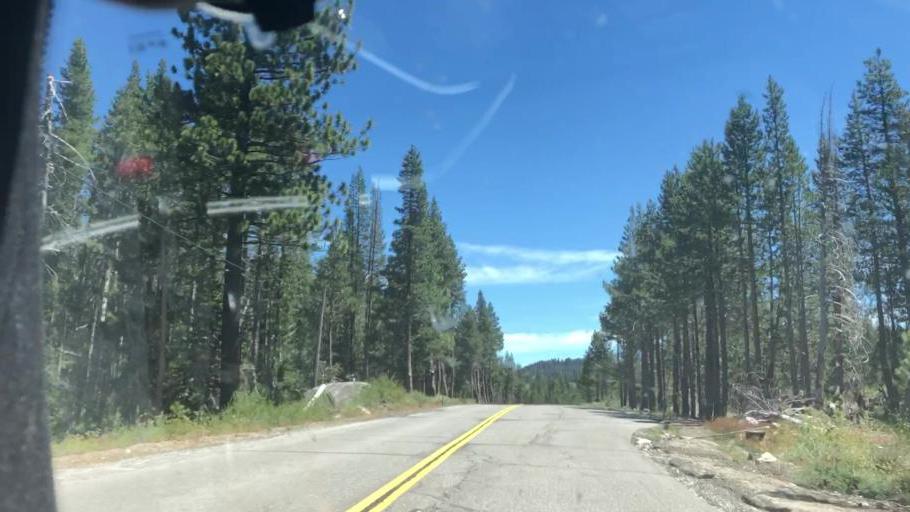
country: US
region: California
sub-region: Nevada County
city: Truckee
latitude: 39.3161
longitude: -120.4630
